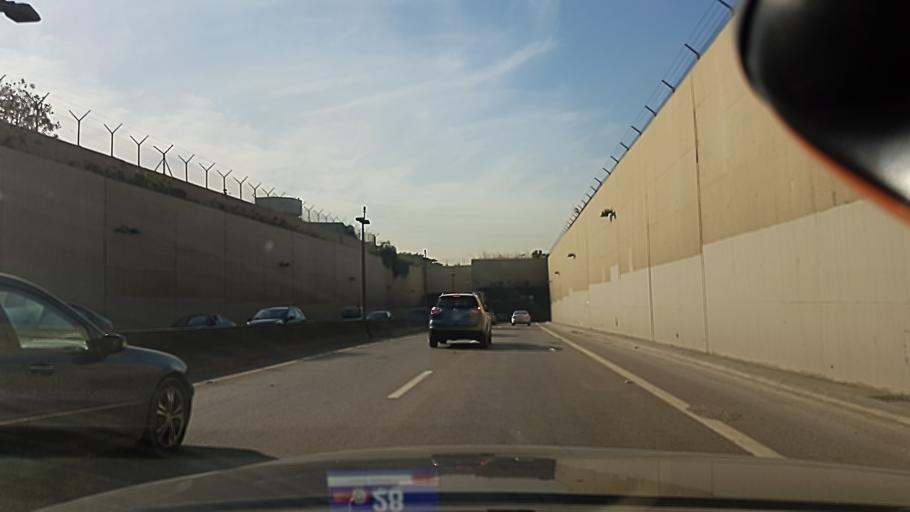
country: LB
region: Mont-Liban
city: Baabda
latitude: 33.8236
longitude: 35.5029
